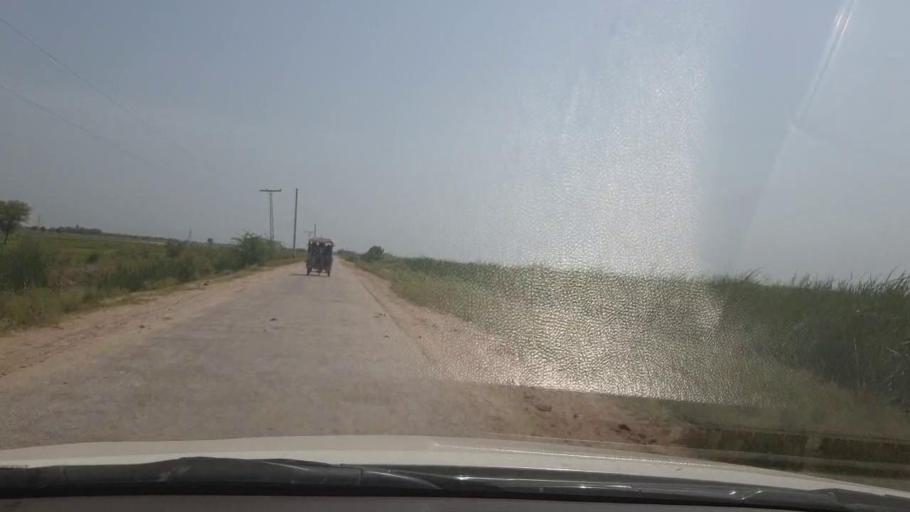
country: PK
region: Sindh
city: Garhi Yasin
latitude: 27.9551
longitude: 68.5055
